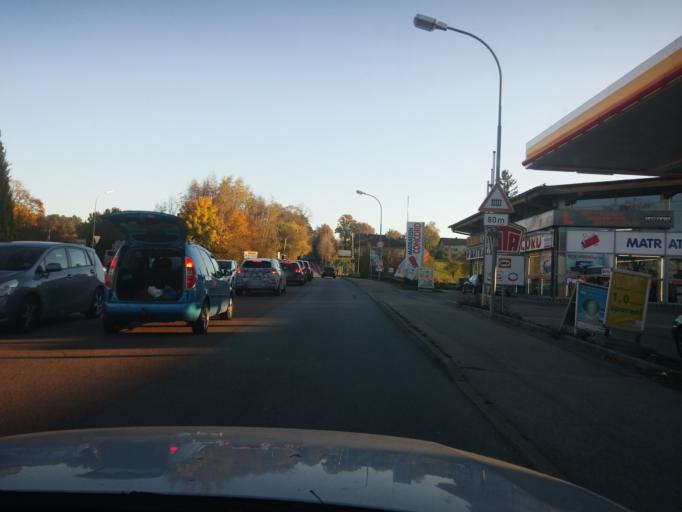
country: DE
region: Bavaria
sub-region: Upper Bavaria
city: Dorfen
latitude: 48.2676
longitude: 12.1551
